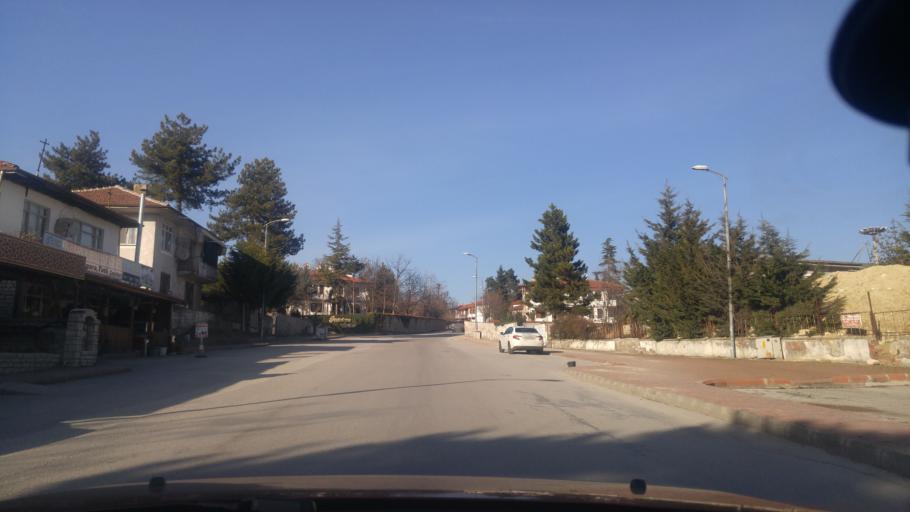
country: TR
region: Karabuk
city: Safranbolu
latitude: 41.2590
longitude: 32.6733
